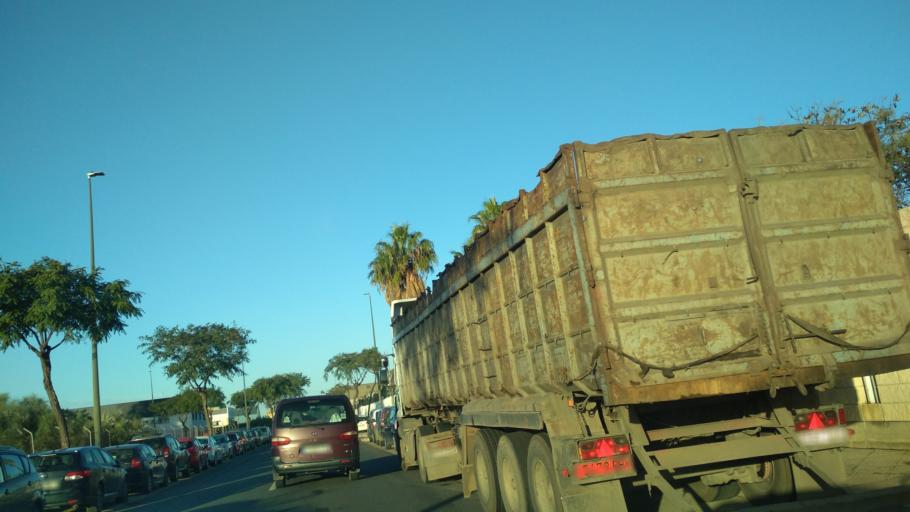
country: ES
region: Andalusia
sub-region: Provincia de Huelva
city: Huelva
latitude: 37.2418
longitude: -6.9463
